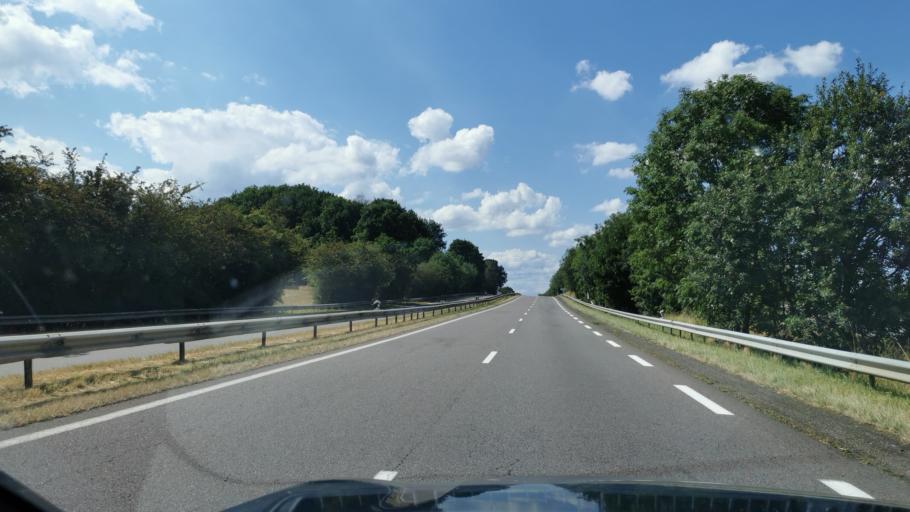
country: FR
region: Lorraine
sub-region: Departement de Meurthe-et-Moselle
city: Hussigny-Godbrange
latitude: 49.4554
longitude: 5.8706
